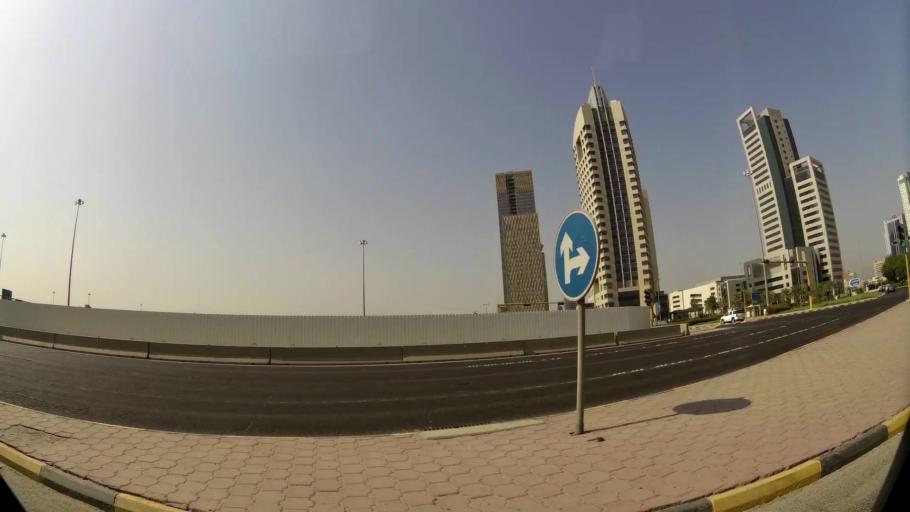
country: KW
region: Al Asimah
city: Kuwait City
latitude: 29.3630
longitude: 47.9861
